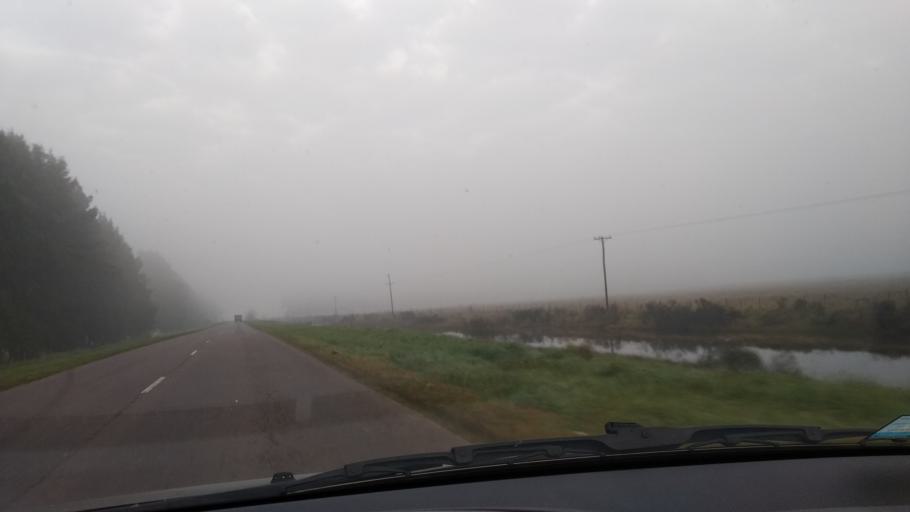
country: AR
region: Buenos Aires
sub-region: Partido de San Vicente
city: San Vicente
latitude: -35.2282
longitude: -58.4502
